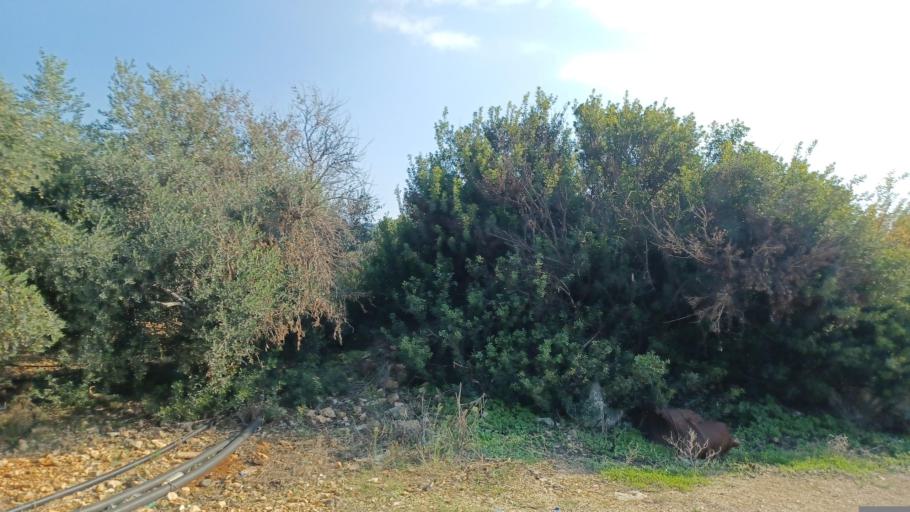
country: CY
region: Pafos
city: Pegeia
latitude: 34.8938
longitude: 32.3309
